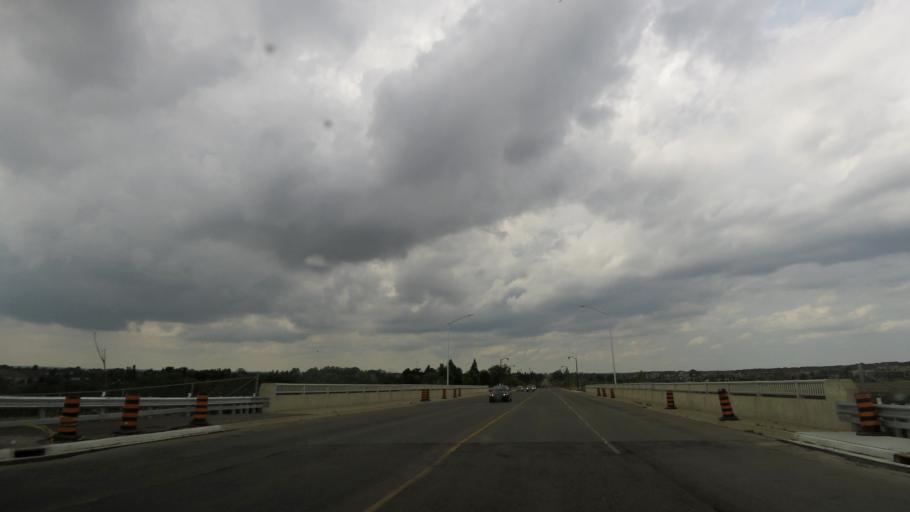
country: CA
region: Ontario
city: Brampton
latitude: 43.7472
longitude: -79.8193
